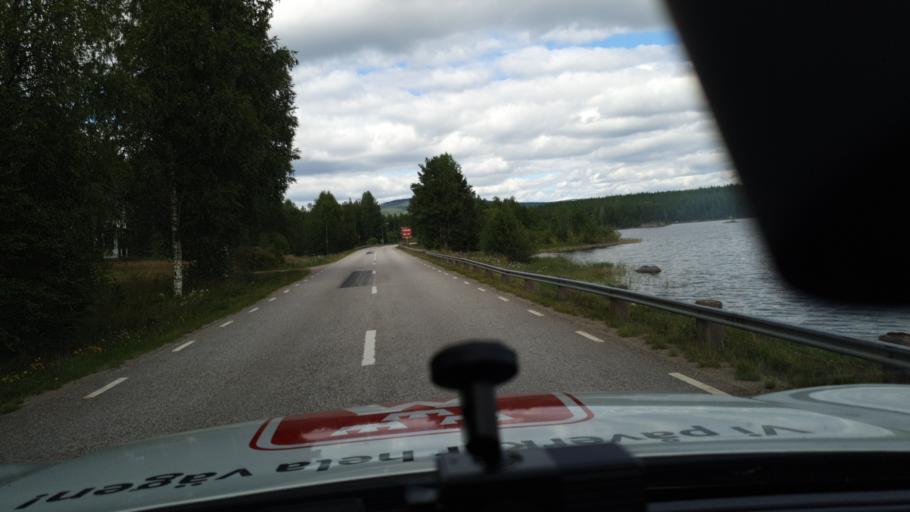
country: NO
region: Hedmark
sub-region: Trysil
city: Innbygda
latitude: 61.0417
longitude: 12.5915
